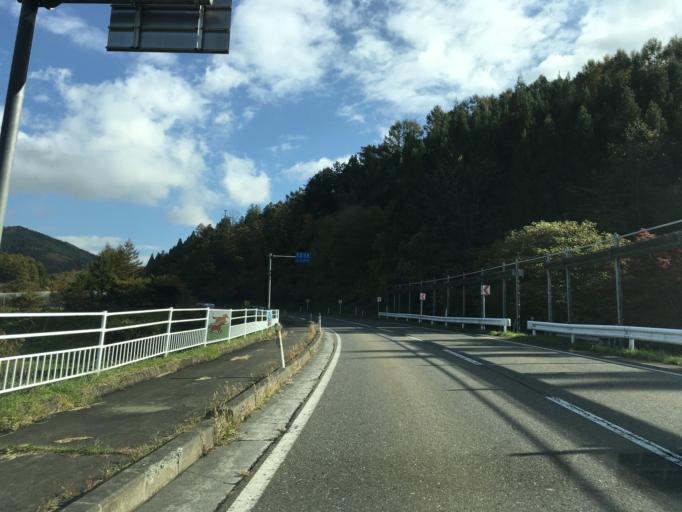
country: JP
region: Iwate
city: Tono
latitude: 39.3633
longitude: 141.4016
